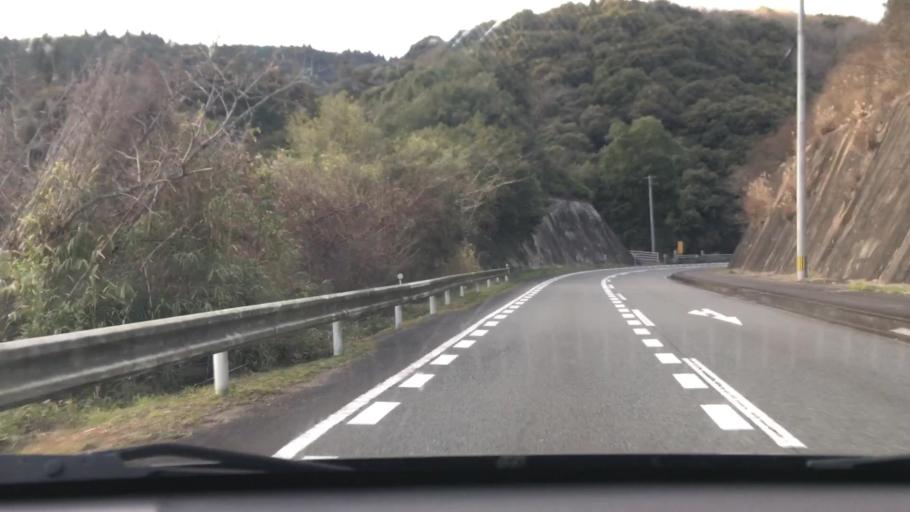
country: JP
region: Oita
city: Hiji
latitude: 33.4231
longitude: 131.4144
